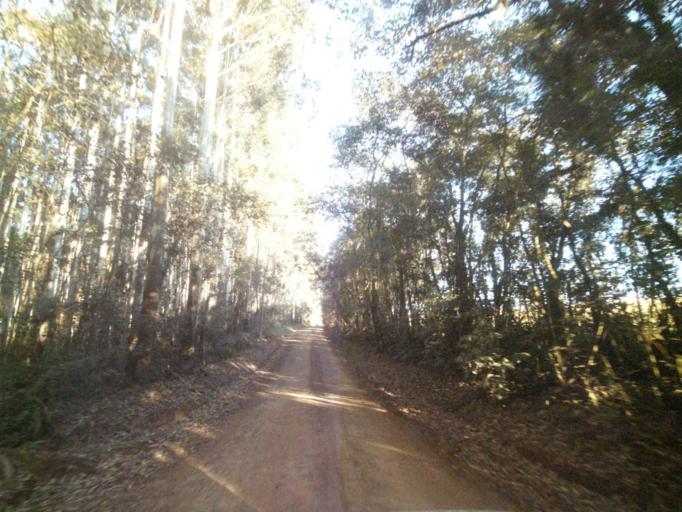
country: BR
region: Parana
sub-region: Telemaco Borba
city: Telemaco Borba
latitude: -24.5129
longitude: -50.6035
